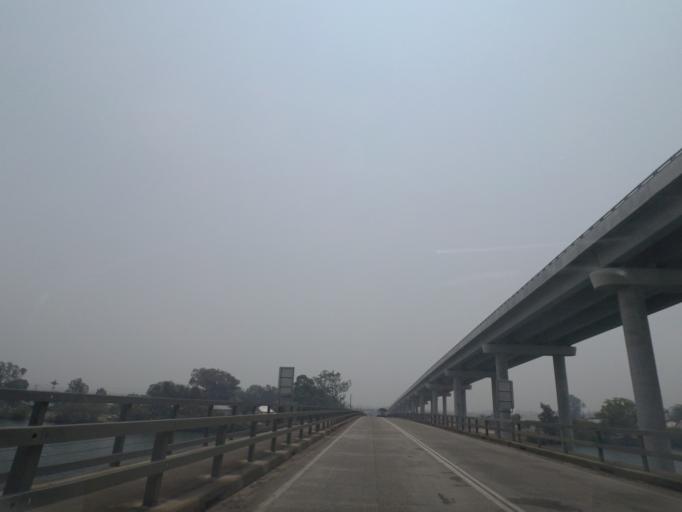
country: AU
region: New South Wales
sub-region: Clarence Valley
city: Maclean
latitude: -29.4286
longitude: 153.2402
